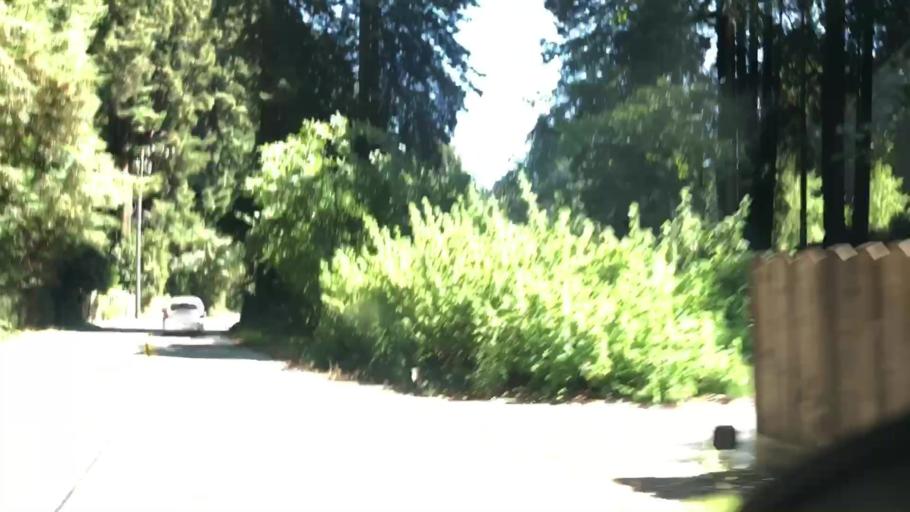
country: US
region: California
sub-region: Santa Cruz County
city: Corralitos
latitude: 37.0146
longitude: -121.8147
